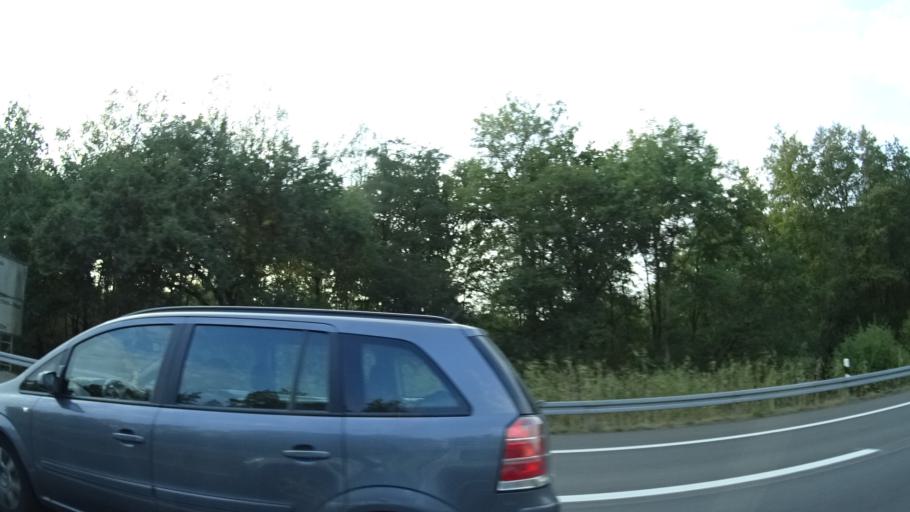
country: DE
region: Hesse
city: Obertshausen
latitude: 50.0778
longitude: 8.8894
